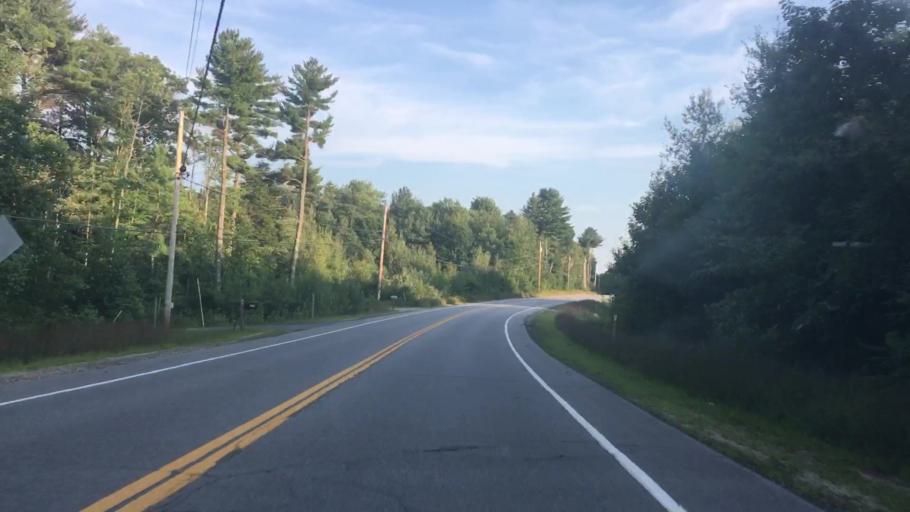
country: US
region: New Hampshire
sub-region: Belknap County
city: Gilmanton
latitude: 43.4384
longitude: -71.4179
